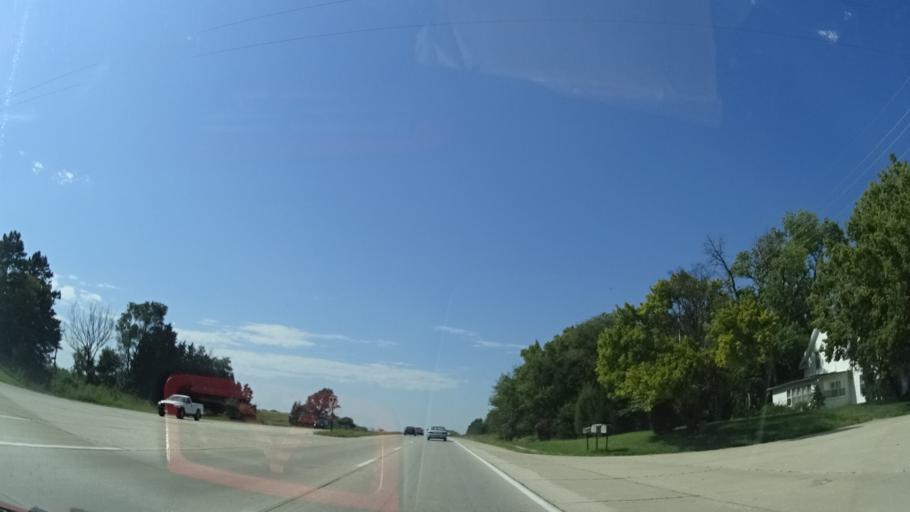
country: US
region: Nebraska
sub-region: Sarpy County
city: Papillion
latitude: 41.1400
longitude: -95.9948
